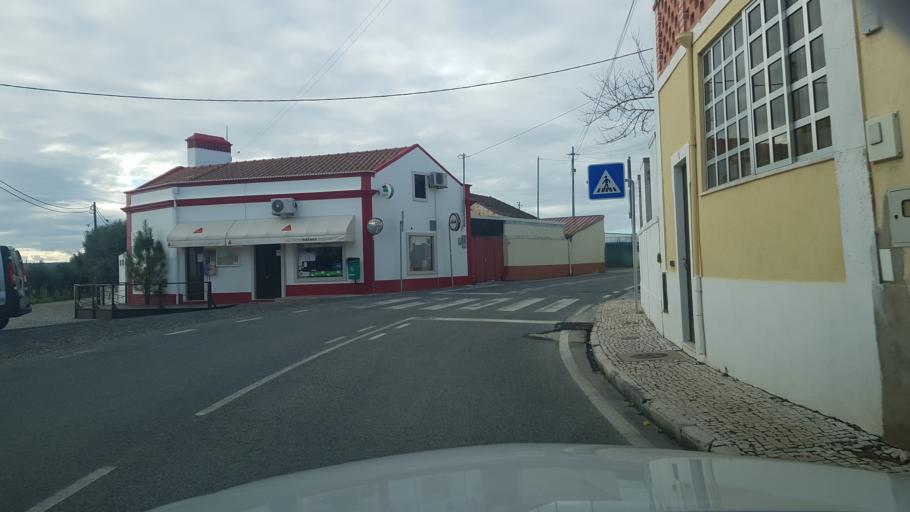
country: PT
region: Santarem
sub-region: Abrantes
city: Tramagal
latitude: 39.4753
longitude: -8.2440
